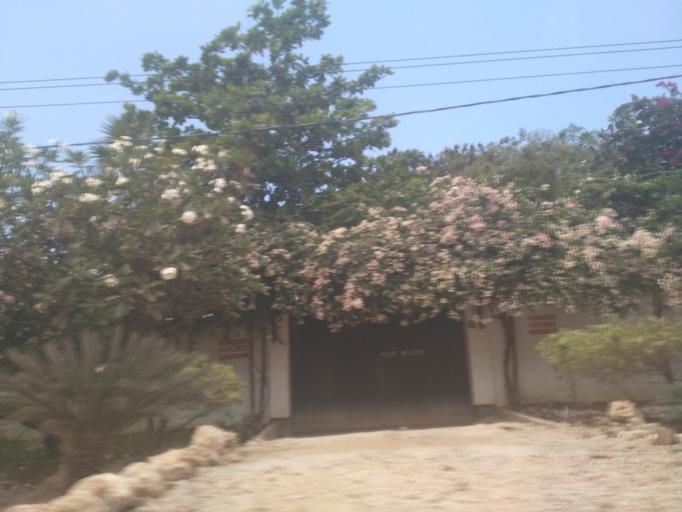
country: TZ
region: Dar es Salaam
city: Magomeni
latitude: -6.7493
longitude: 39.2784
